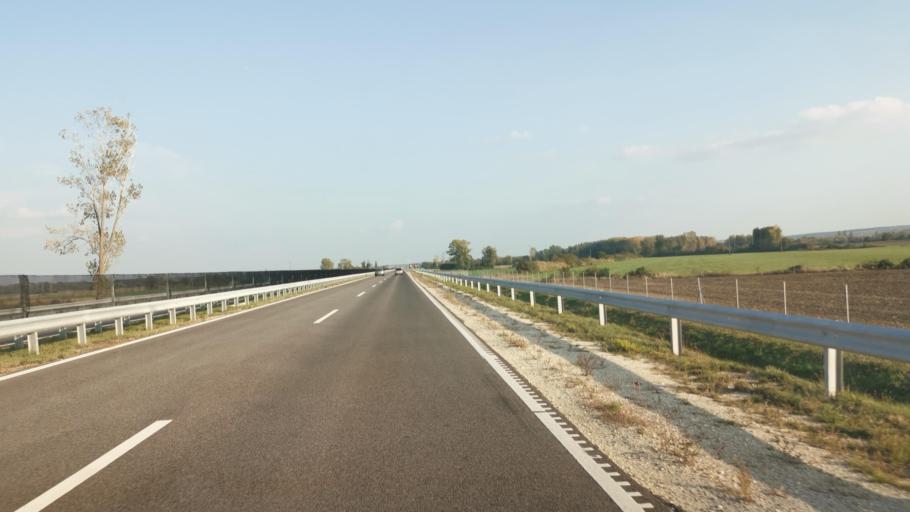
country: HU
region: Gyor-Moson-Sopron
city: Nagycenk
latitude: 47.5784
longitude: 16.7629
